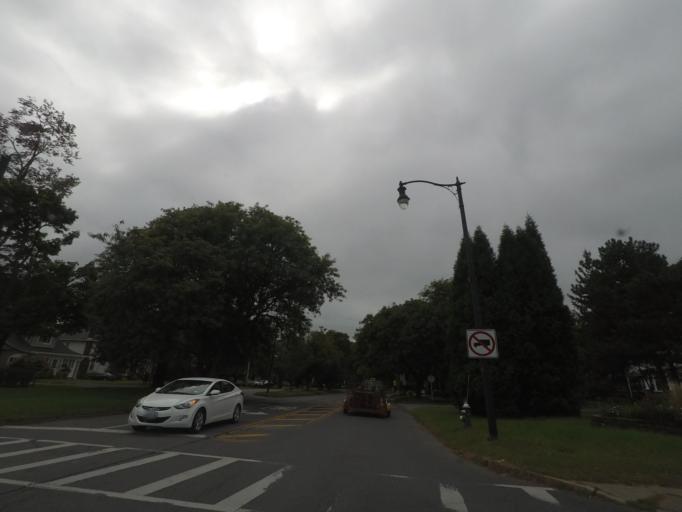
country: US
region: New York
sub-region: Albany County
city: West Albany
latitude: 42.6728
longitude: -73.7907
